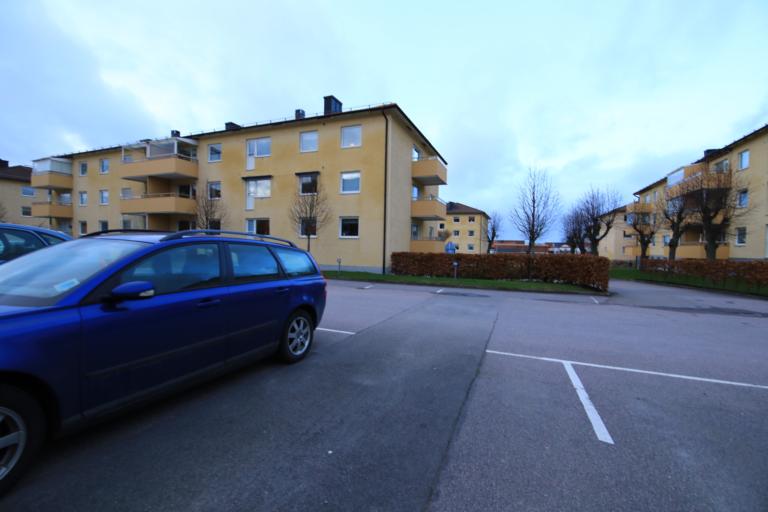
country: SE
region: Halland
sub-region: Varbergs Kommun
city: Varberg
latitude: 57.0950
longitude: 12.2511
